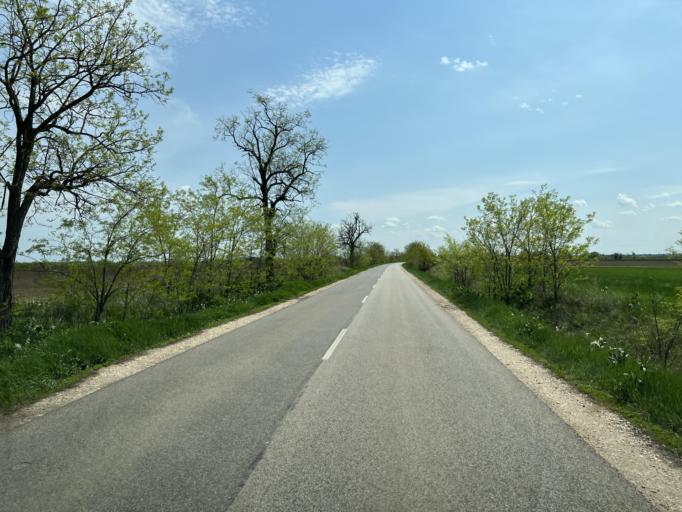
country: HU
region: Pest
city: Tapioszentmarton
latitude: 47.3103
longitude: 19.7600
